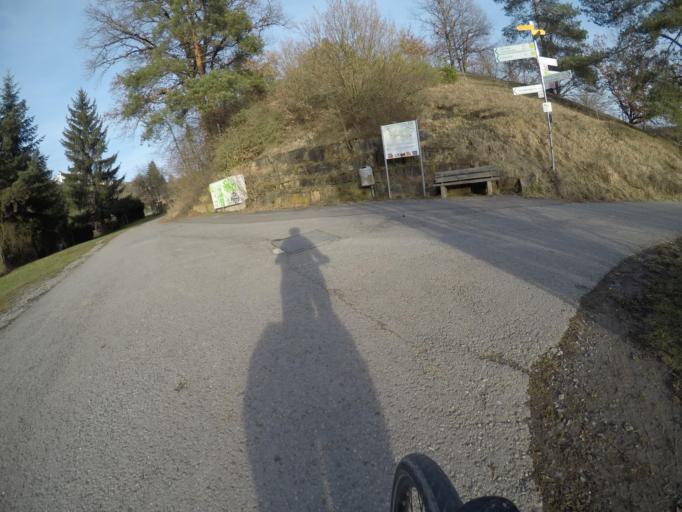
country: DE
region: Baden-Wuerttemberg
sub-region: Regierungsbezirk Stuttgart
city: Schonaich
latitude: 48.6510
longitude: 9.0584
